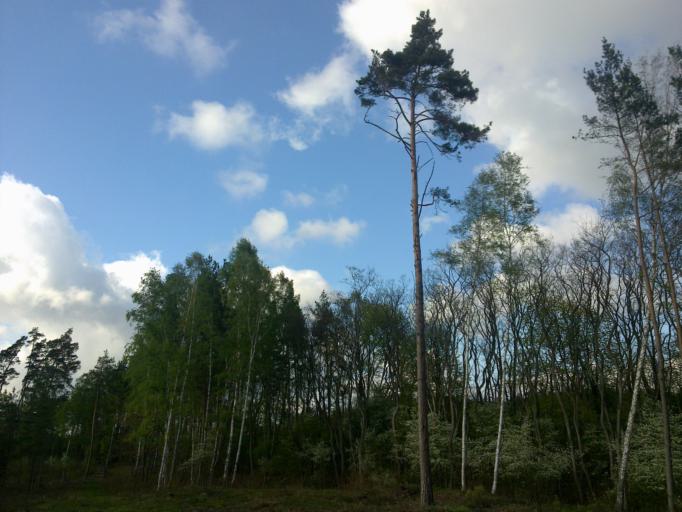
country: PL
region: Pomeranian Voivodeship
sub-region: Powiat sztumski
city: Sztum
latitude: 53.9512
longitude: 19.0012
